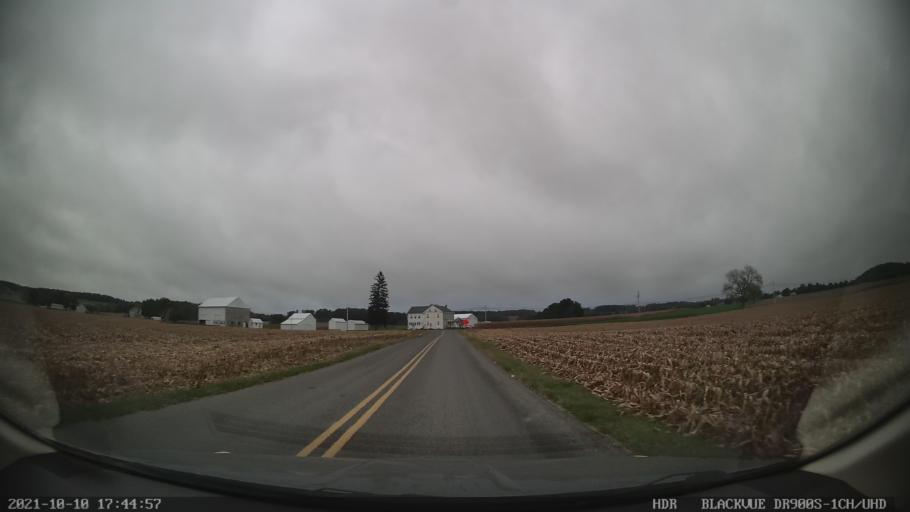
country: US
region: Pennsylvania
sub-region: Lehigh County
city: Breinigsville
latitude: 40.5493
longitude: -75.6767
